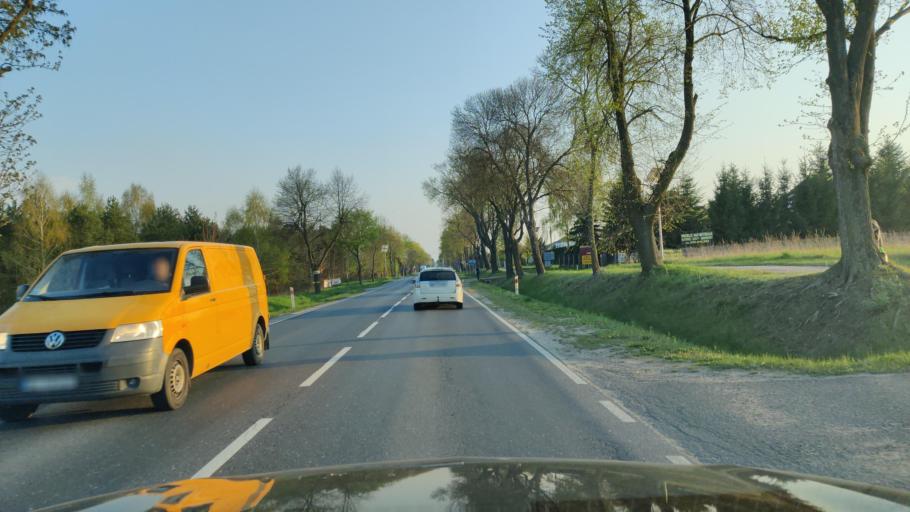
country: PL
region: Masovian Voivodeship
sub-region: Powiat legionowski
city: Serock
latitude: 52.5729
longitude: 21.0911
